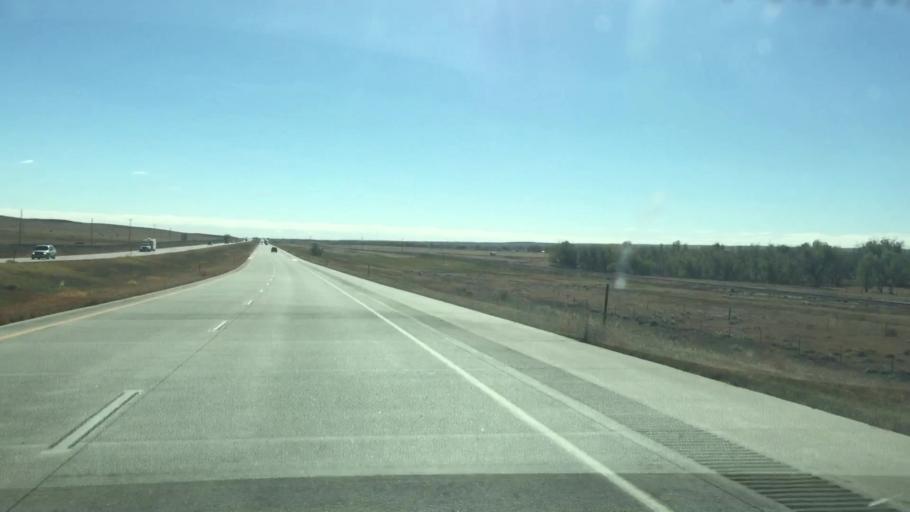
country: US
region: Colorado
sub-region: Lincoln County
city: Limon
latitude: 39.3021
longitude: -103.8145
